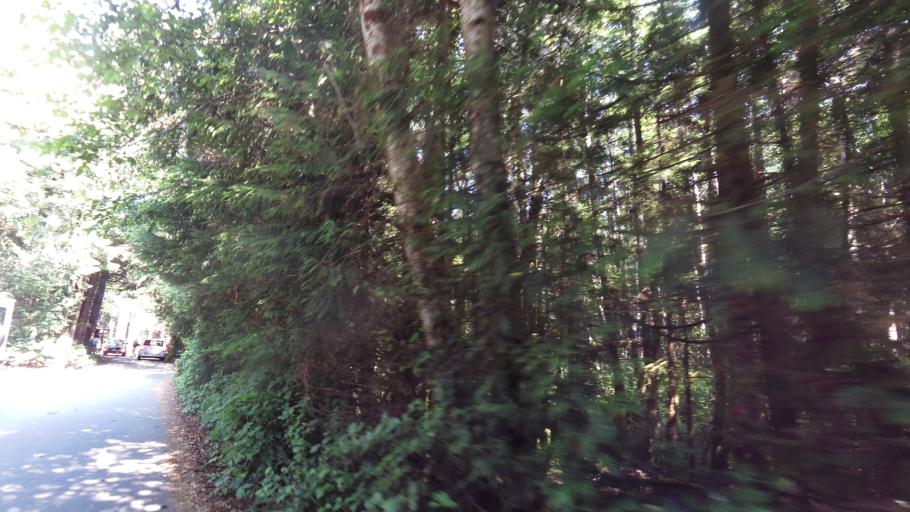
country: CA
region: British Columbia
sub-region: Regional District of Alberni-Clayoquot
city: Ucluelet
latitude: 49.0416
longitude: -125.6812
